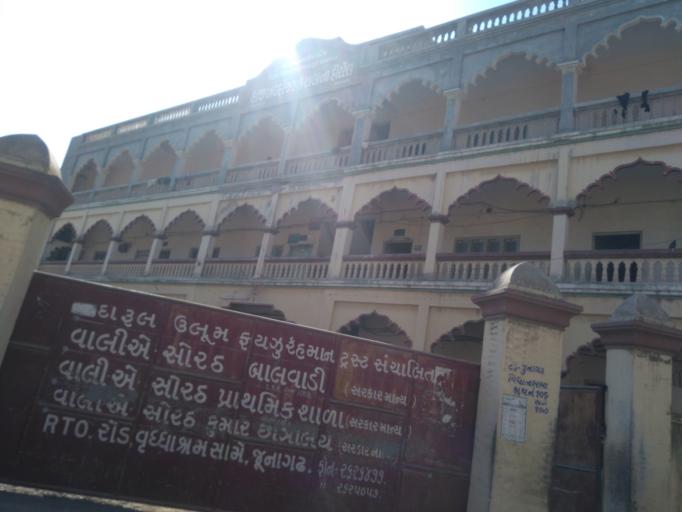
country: IN
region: Gujarat
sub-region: Junagadh
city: Junagadh
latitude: 21.5304
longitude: 70.4629
